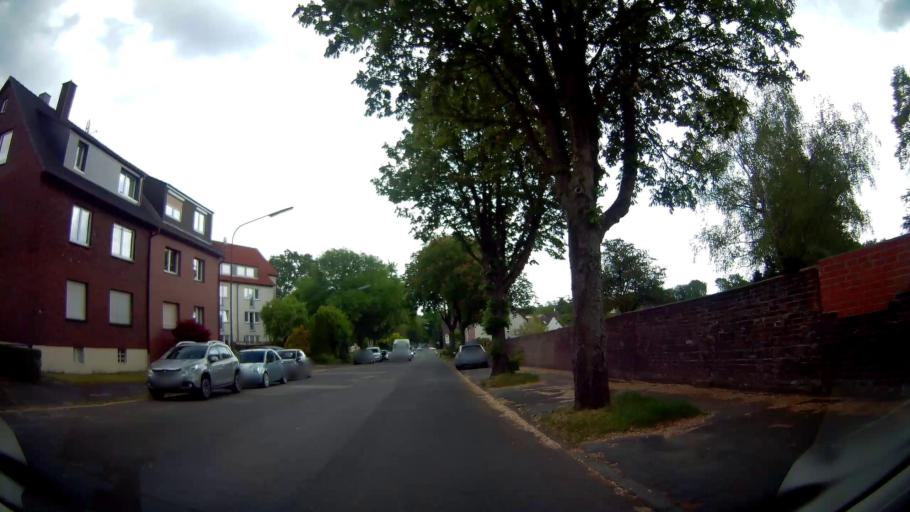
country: DE
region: North Rhine-Westphalia
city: Bochum-Hordel
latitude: 51.5090
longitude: 7.1777
